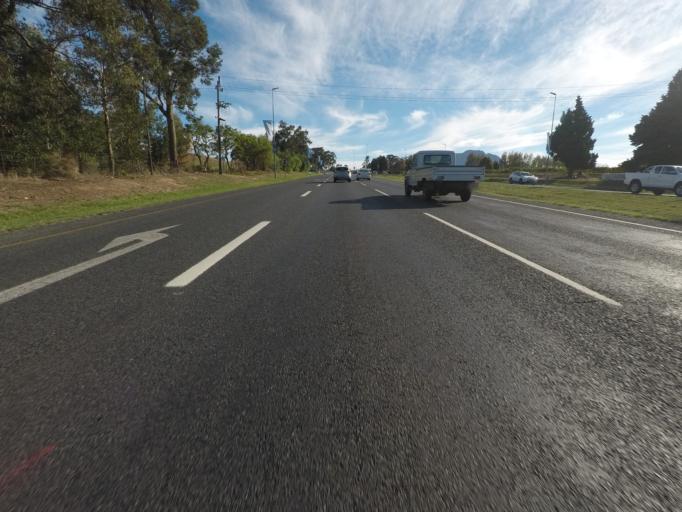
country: ZA
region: Western Cape
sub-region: Cape Winelands District Municipality
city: Stellenbosch
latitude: -33.9705
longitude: 18.8436
